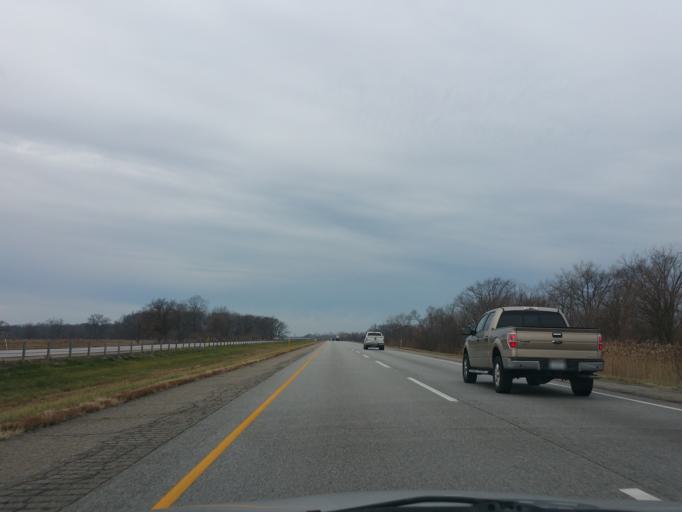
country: US
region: Indiana
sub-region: Porter County
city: Chesterton
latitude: 41.5797
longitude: -87.0777
